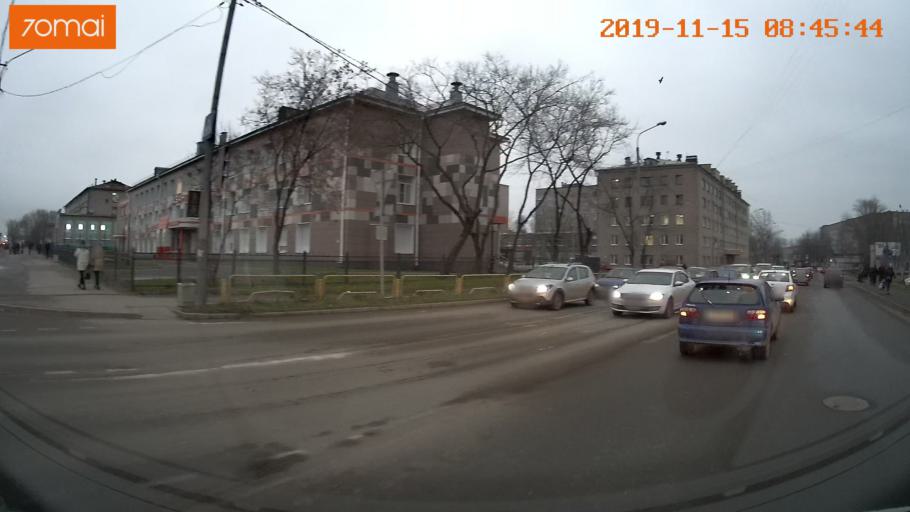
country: RU
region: Vologda
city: Cherepovets
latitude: 59.1190
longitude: 37.9033
